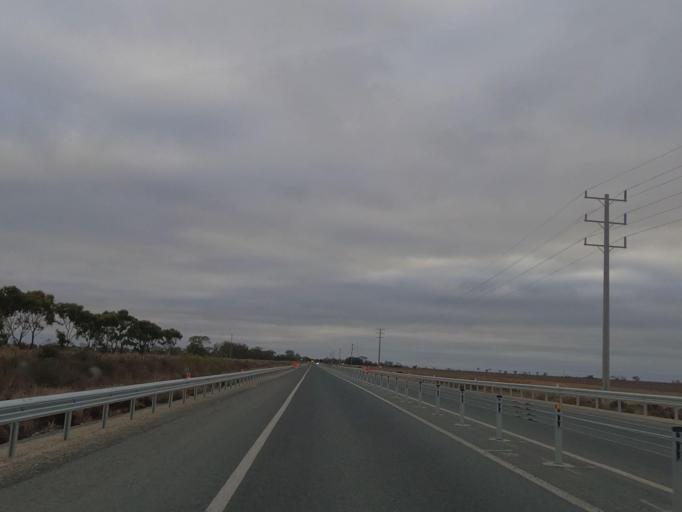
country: AU
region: Victoria
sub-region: Swan Hill
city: Swan Hill
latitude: -35.5432
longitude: 143.7566
